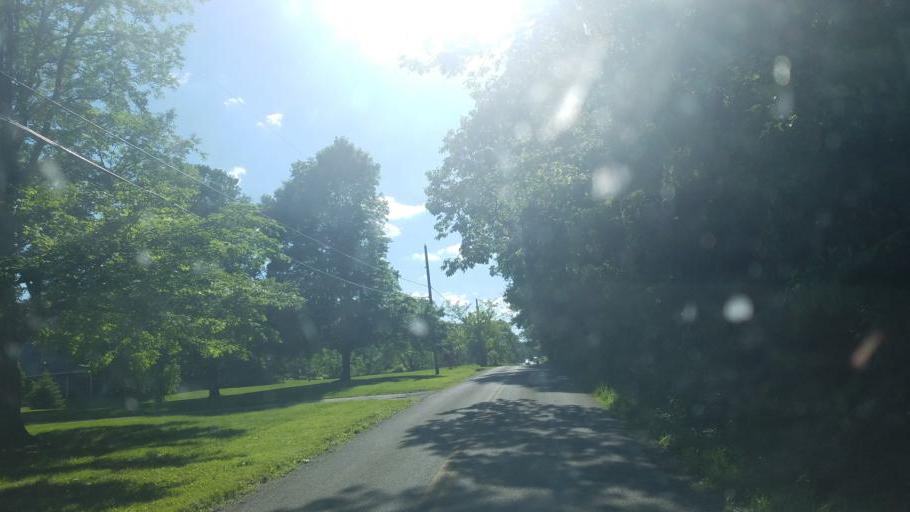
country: US
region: Ohio
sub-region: Richland County
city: Lincoln Heights
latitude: 40.7861
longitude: -82.4272
